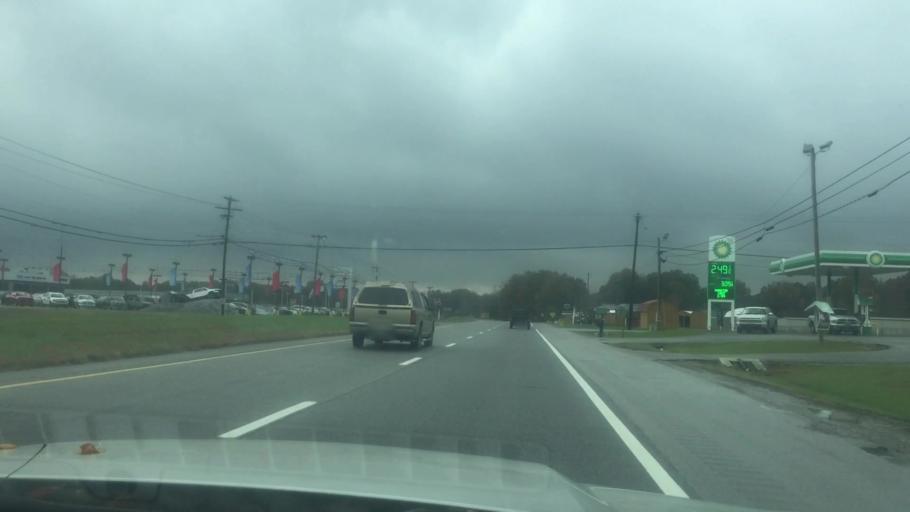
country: US
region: Tennessee
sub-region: Coffee County
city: Tullahoma
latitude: 35.3672
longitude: -86.1905
